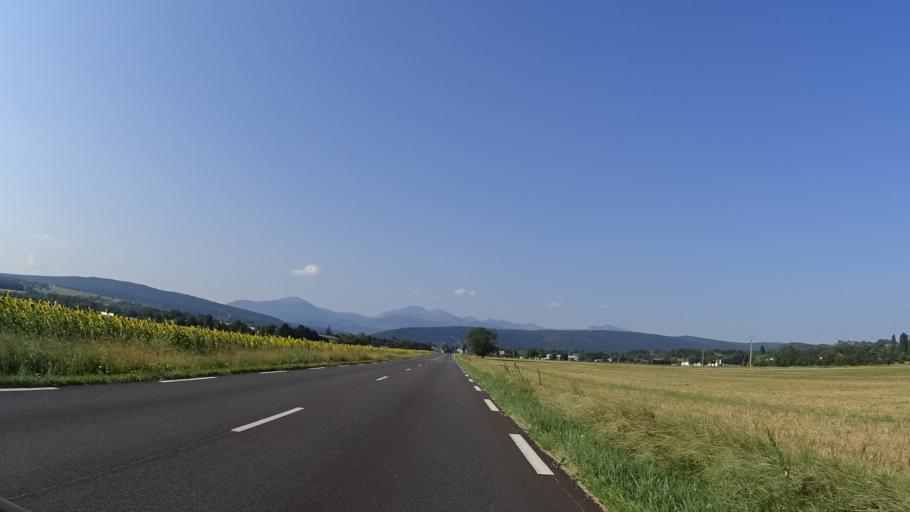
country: FR
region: Midi-Pyrenees
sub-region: Departement de l'Ariege
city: Lavelanet
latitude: 42.9897
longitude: 1.8752
